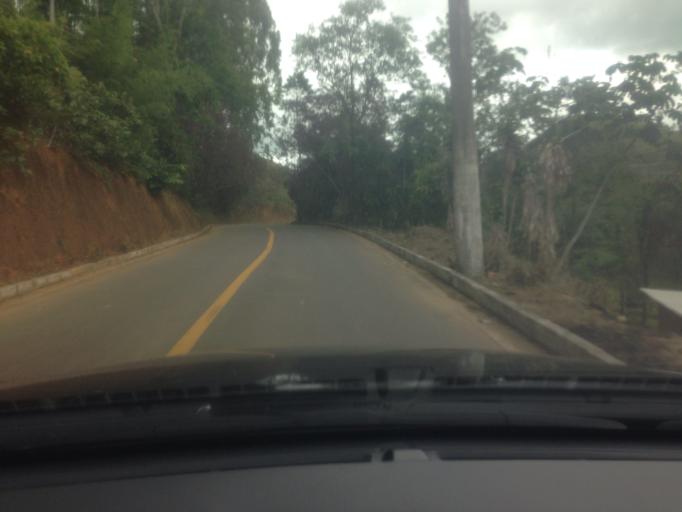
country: BR
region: Espirito Santo
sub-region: Guarapari
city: Guarapari
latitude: -20.5561
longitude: -40.5550
